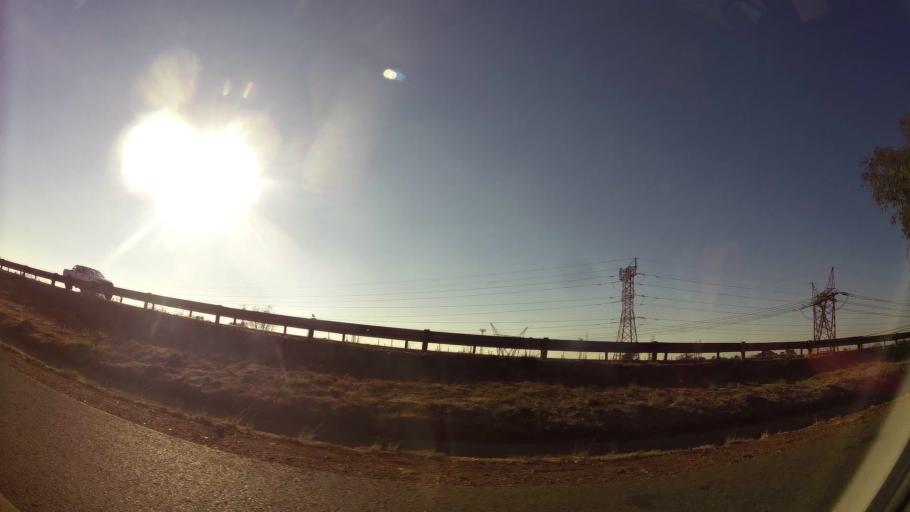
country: ZA
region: Gauteng
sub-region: Ekurhuleni Metropolitan Municipality
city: Germiston
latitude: -26.3076
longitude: 28.1125
